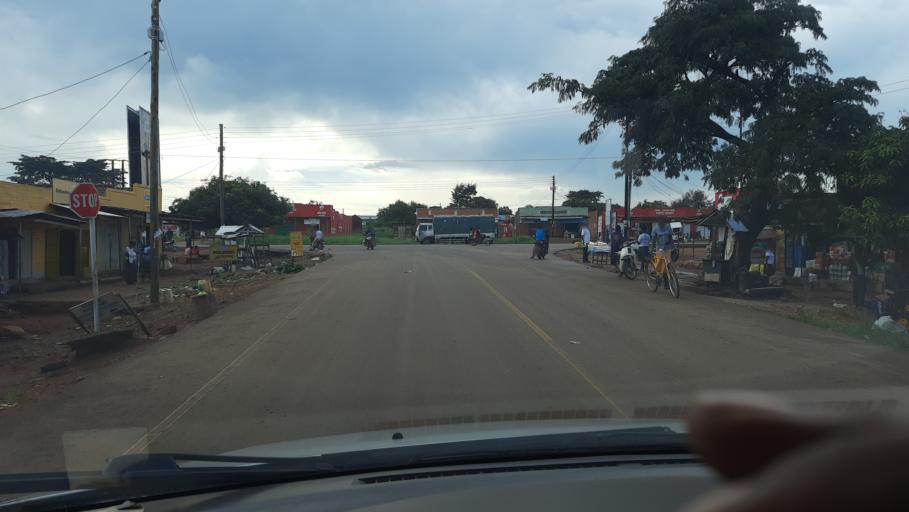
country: UG
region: Central Region
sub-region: Nakasongola District
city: Nakasongola
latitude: 1.3258
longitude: 32.4228
